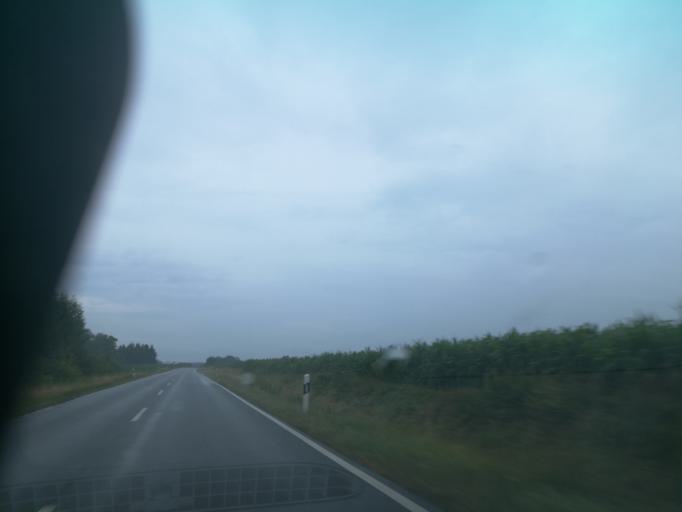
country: DE
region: Bavaria
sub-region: Regierungsbezirk Mittelfranken
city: Obermichelbach
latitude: 49.5309
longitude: 10.9361
